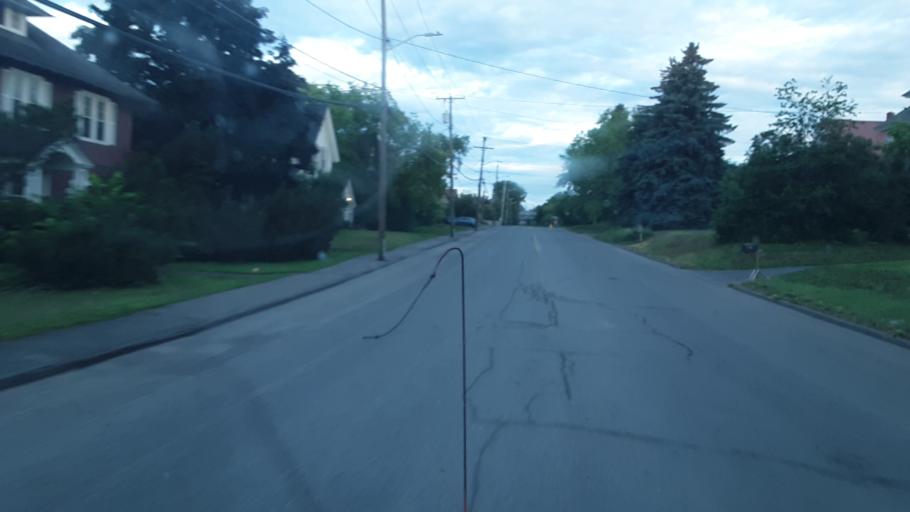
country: US
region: Maine
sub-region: Aroostook County
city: Presque Isle
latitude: 46.6854
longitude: -68.0163
